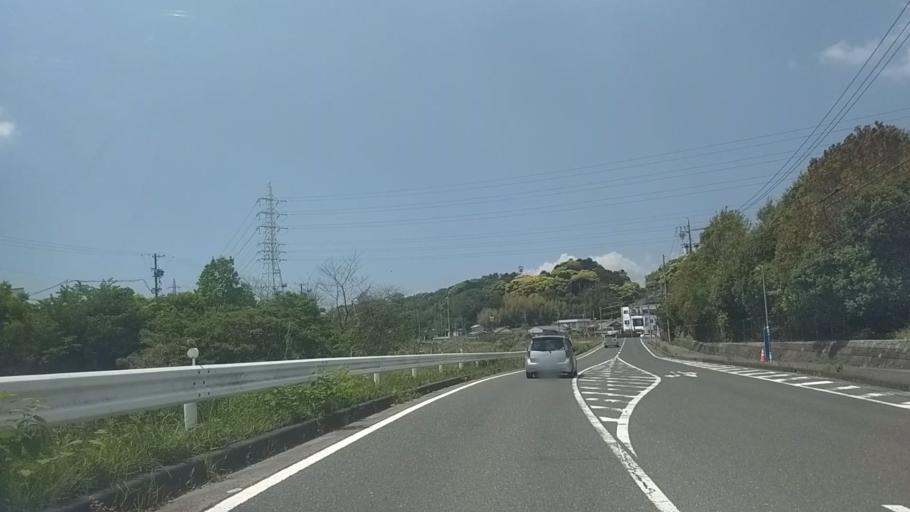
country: JP
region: Shizuoka
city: Hamamatsu
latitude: 34.7718
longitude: 137.6710
